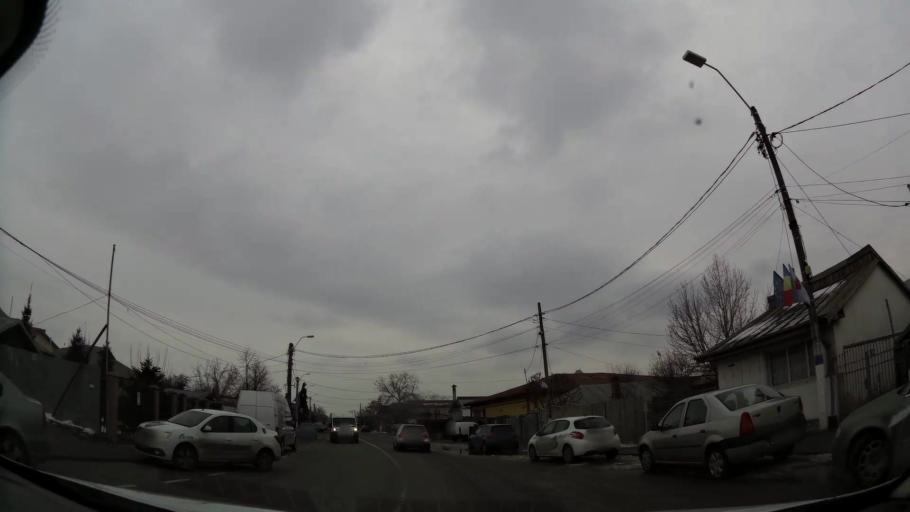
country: RO
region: Ilfov
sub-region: Comuna Tunari
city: Tunari
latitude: 44.5498
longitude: 26.1454
